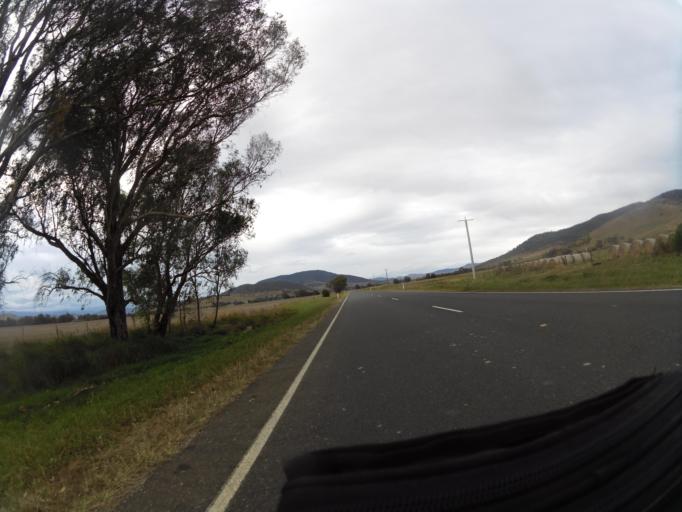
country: AU
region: New South Wales
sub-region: Snowy River
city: Jindabyne
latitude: -36.1029
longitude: 147.9806
